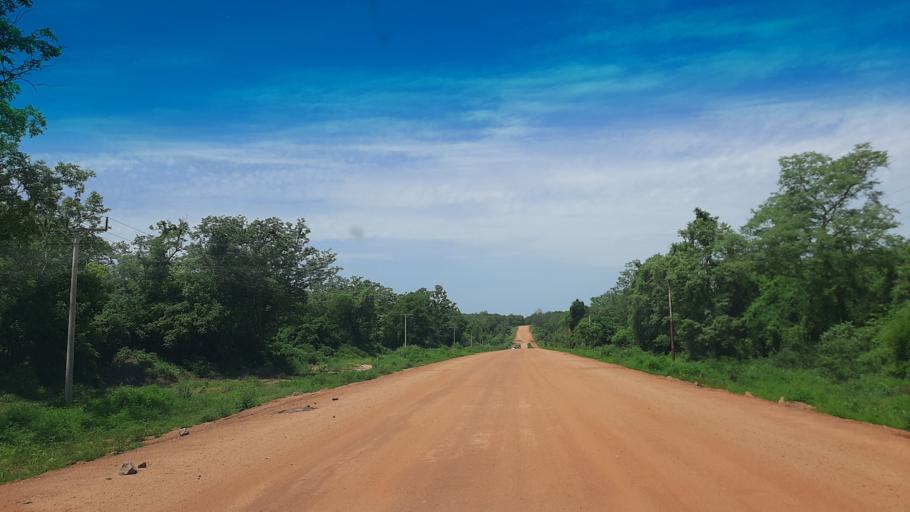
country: ET
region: Gambela
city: Gambela
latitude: 8.0929
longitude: 34.5888
